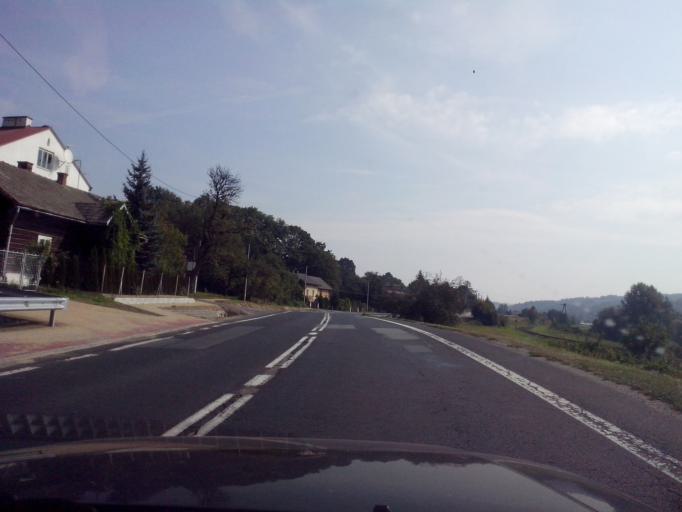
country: PL
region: Subcarpathian Voivodeship
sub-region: Powiat strzyzowski
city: Babica
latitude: 49.9363
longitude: 21.8839
